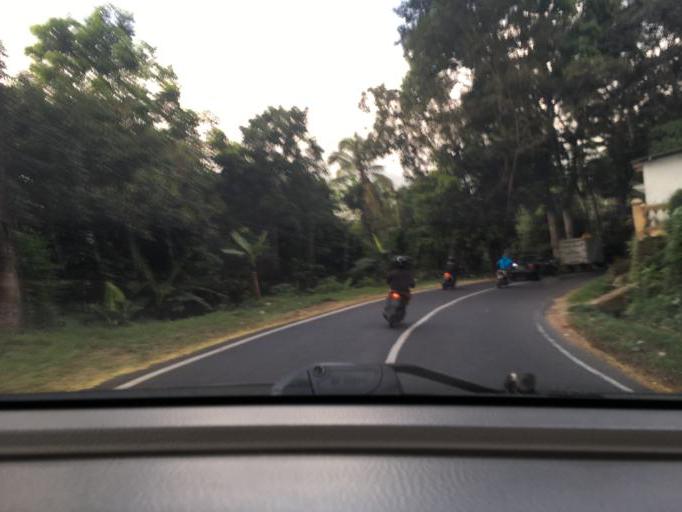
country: ID
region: West Java
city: Kaliwon Kertawirama
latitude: -7.0116
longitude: 108.4326
